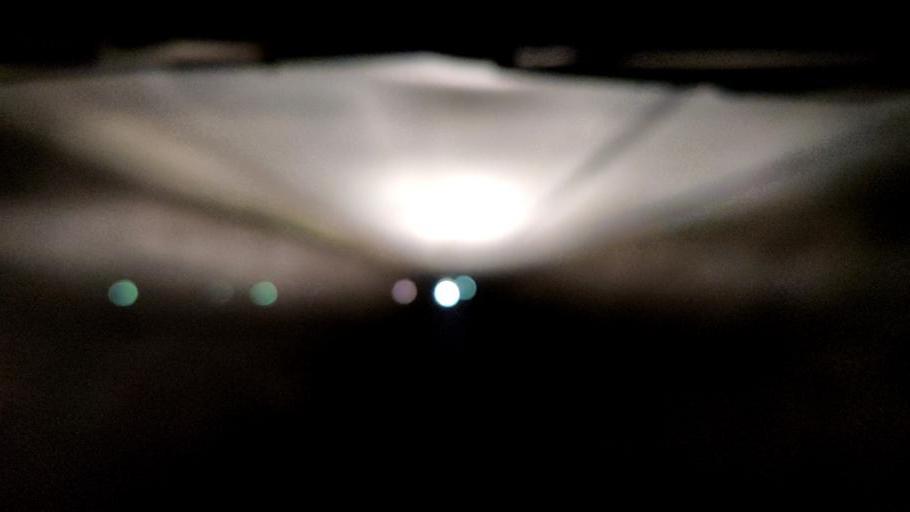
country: RU
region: Voronezj
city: Podkletnoye
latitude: 51.6408
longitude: 39.4954
